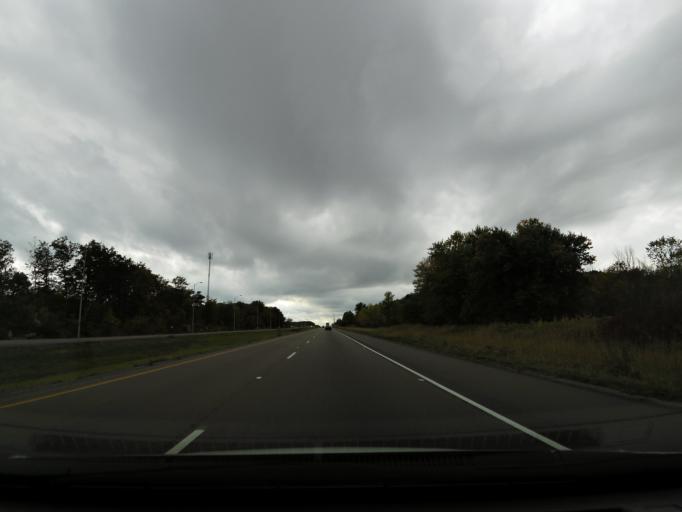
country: CA
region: Ontario
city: Gananoque
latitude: 44.3643
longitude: -76.0725
